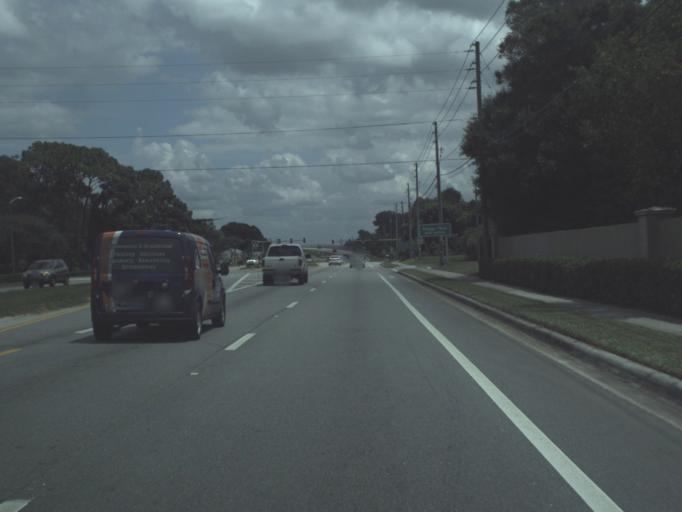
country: US
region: Florida
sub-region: Pinellas County
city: Oldsmar
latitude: 28.0269
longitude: -82.6981
